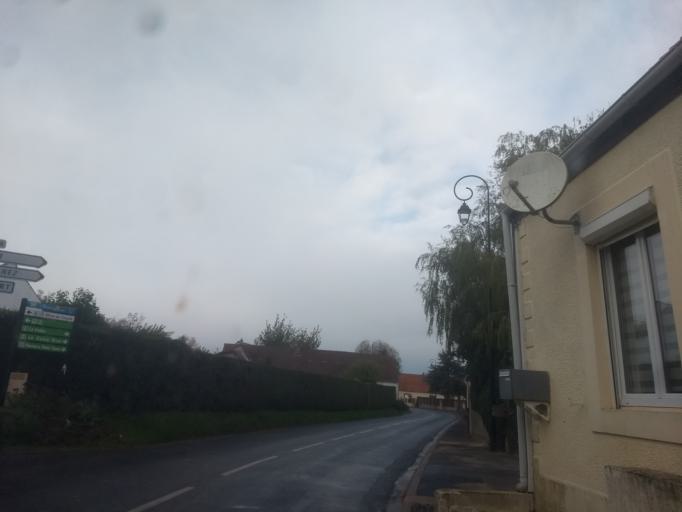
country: FR
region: Nord-Pas-de-Calais
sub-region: Departement du Pas-de-Calais
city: Wissant
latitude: 50.8823
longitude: 1.7112
